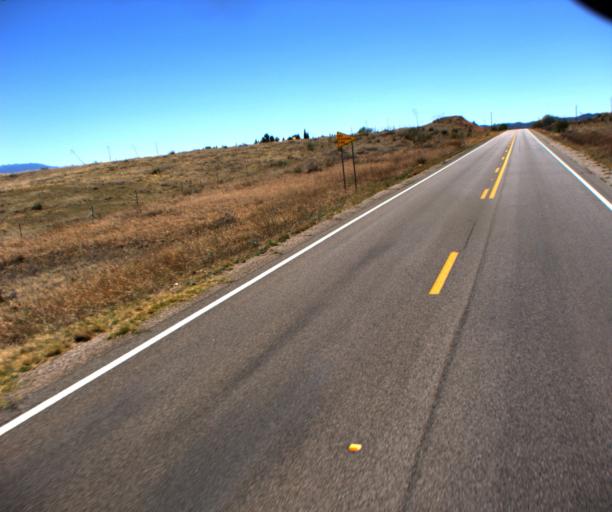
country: US
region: Arizona
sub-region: Pima County
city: Corona de Tucson
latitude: 31.7008
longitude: -110.6554
